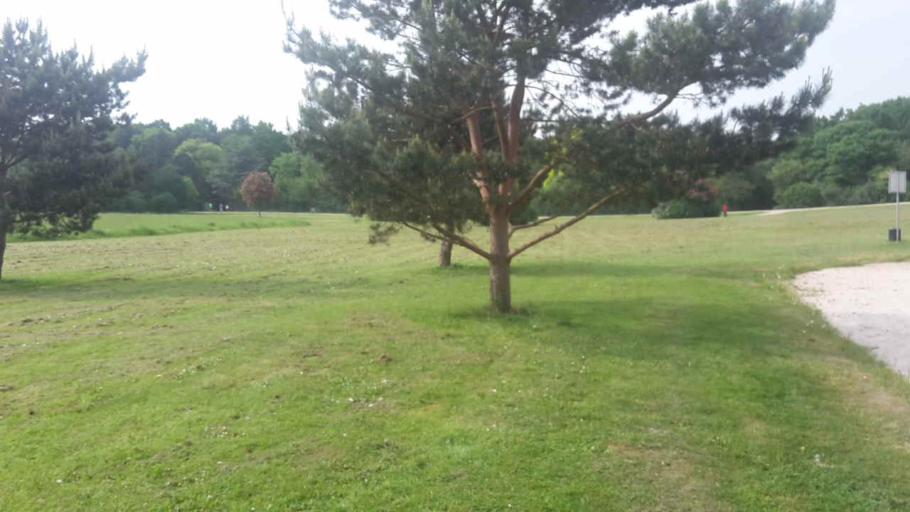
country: DE
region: North Rhine-Westphalia
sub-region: Regierungsbezirk Koln
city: Poll
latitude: 50.8819
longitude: 6.9837
